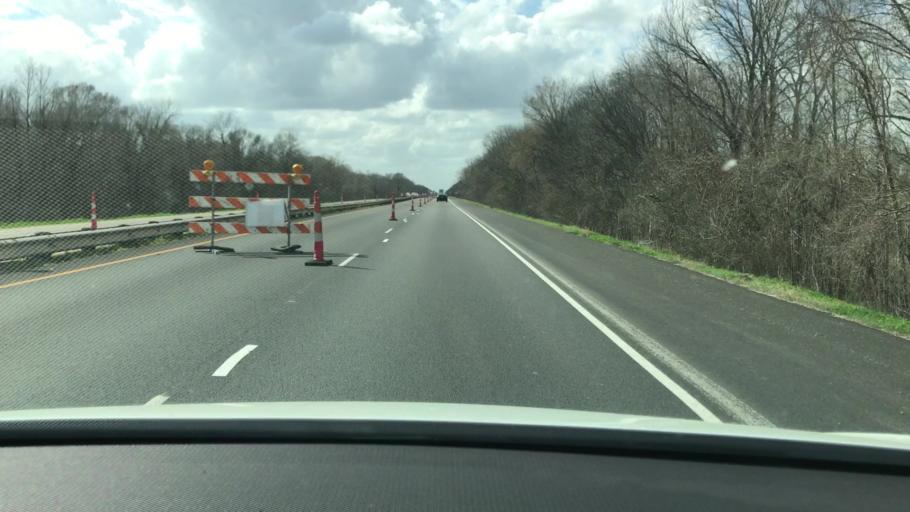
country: US
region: Louisiana
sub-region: Saint Landry Parish
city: Krotz Springs
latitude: 30.5568
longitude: -91.6590
